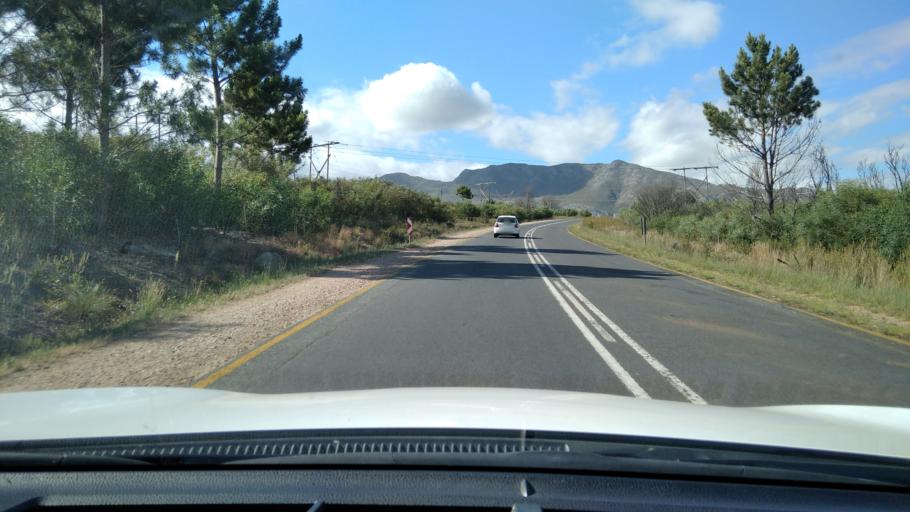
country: ZA
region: Western Cape
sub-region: Overberg District Municipality
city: Hermanus
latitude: -34.2423
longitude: 19.1848
